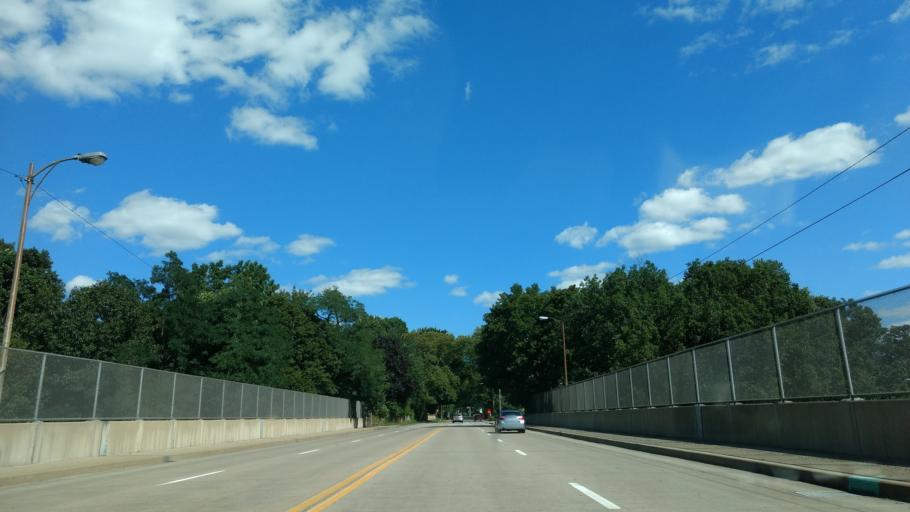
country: US
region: Pennsylvania
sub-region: Allegheny County
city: Ben Avon
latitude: 40.5028
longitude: -80.0788
